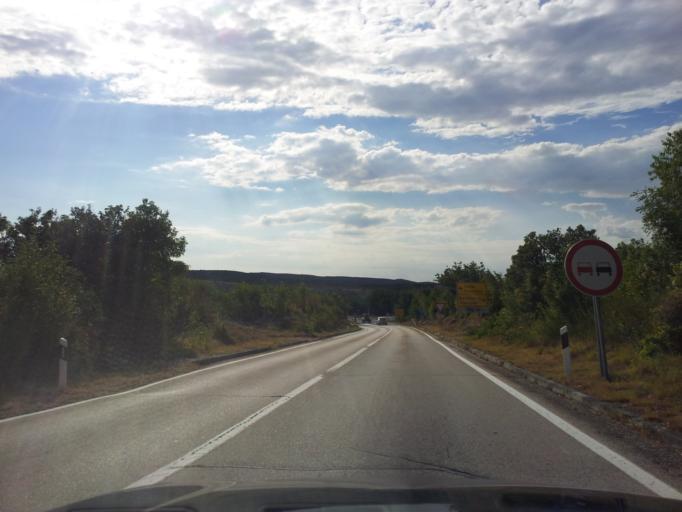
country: HR
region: Zadarska
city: Posedarje
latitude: 44.2294
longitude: 15.5340
